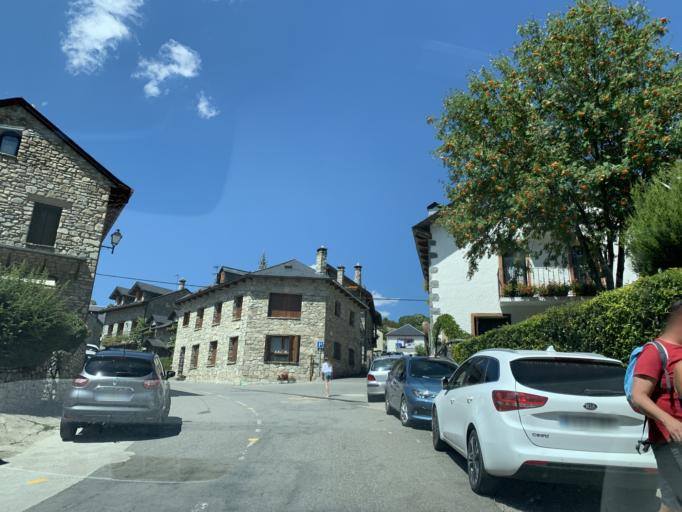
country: ES
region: Aragon
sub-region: Provincia de Huesca
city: Hoz de Jaca
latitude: 42.6898
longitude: -0.3056
